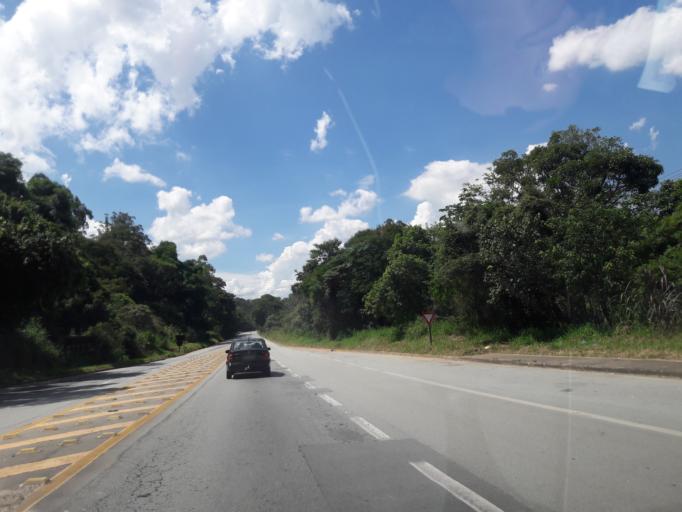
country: BR
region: Sao Paulo
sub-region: Francisco Morato
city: Francisco Morato
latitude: -23.3024
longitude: -46.8104
